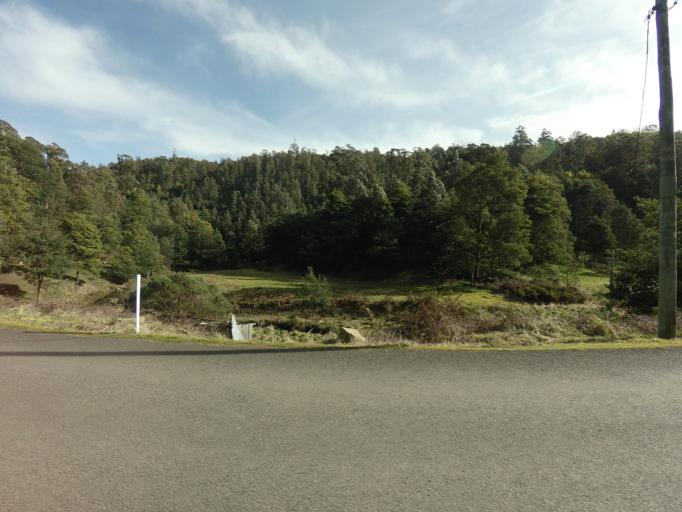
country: AU
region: Tasmania
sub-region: Huon Valley
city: Huonville
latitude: -43.0364
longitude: 147.1418
